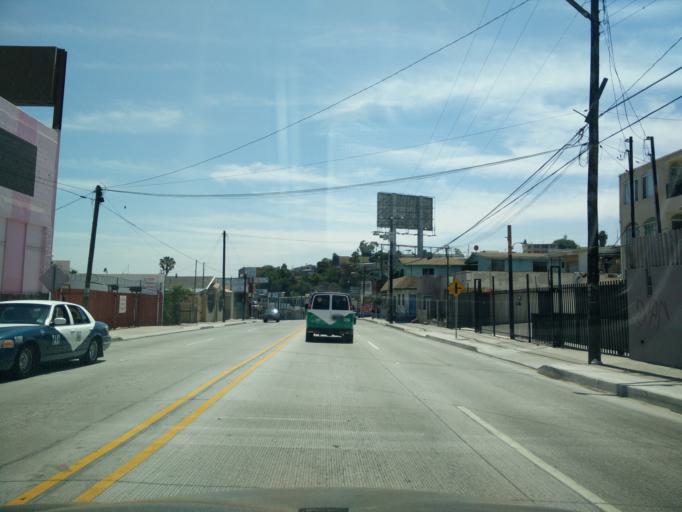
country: MX
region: Baja California
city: Tijuana
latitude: 32.5341
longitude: -117.0568
